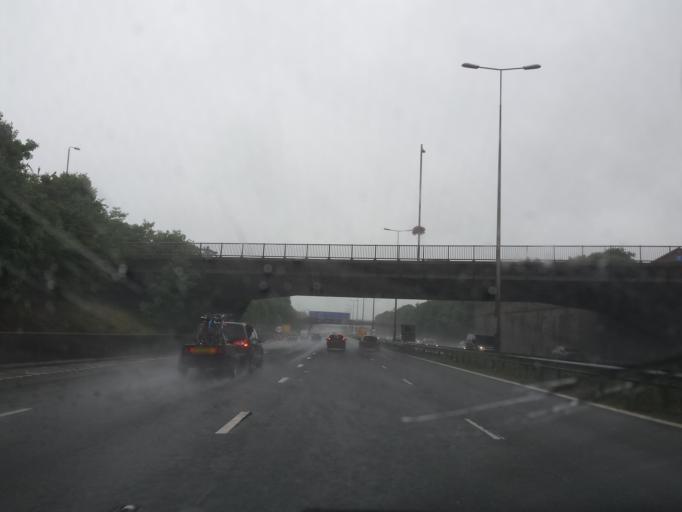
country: GB
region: England
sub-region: Leicestershire
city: Kirby Muxloe
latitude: 52.6258
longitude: -1.2105
